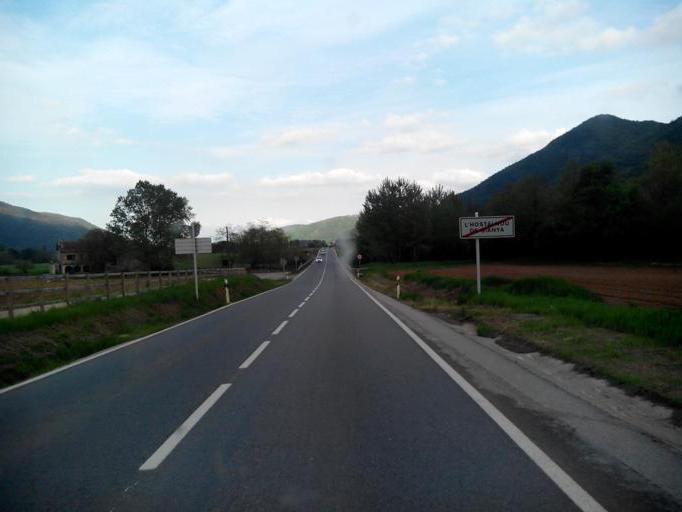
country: ES
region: Catalonia
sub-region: Provincia de Girona
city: MeteOlot
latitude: 42.2108
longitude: 2.4561
